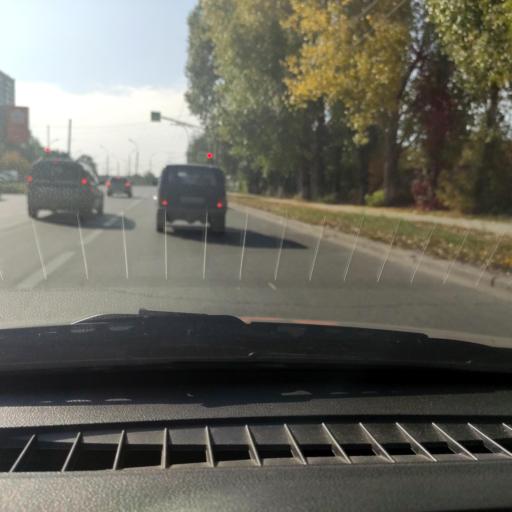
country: RU
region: Samara
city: Tol'yatti
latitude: 53.5134
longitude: 49.2572
